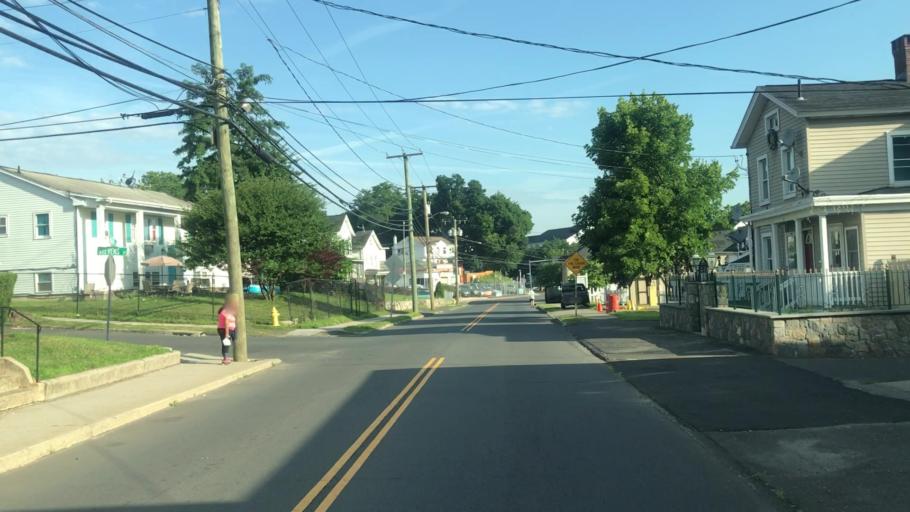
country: US
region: Connecticut
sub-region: Fairfield County
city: Danbury
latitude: 41.3941
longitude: -73.4563
